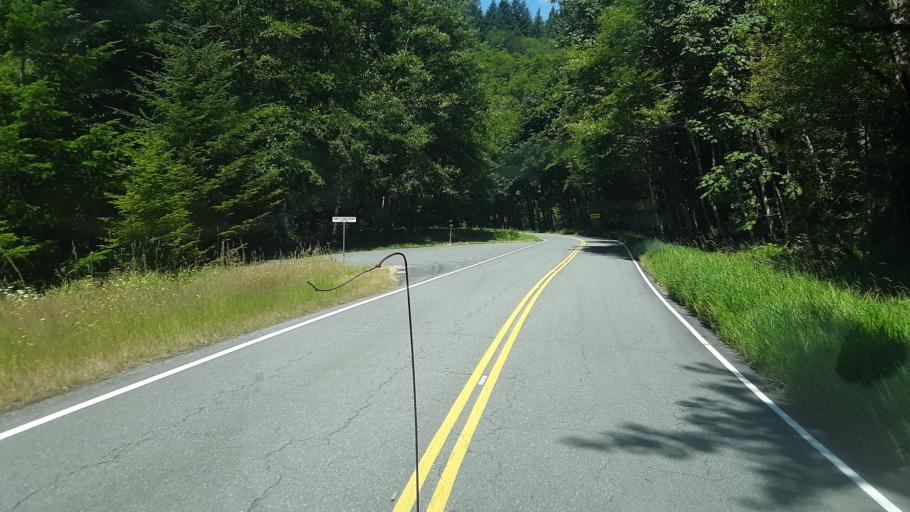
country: US
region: Washington
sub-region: Clark County
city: Yacolt
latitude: 46.0664
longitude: -122.2040
